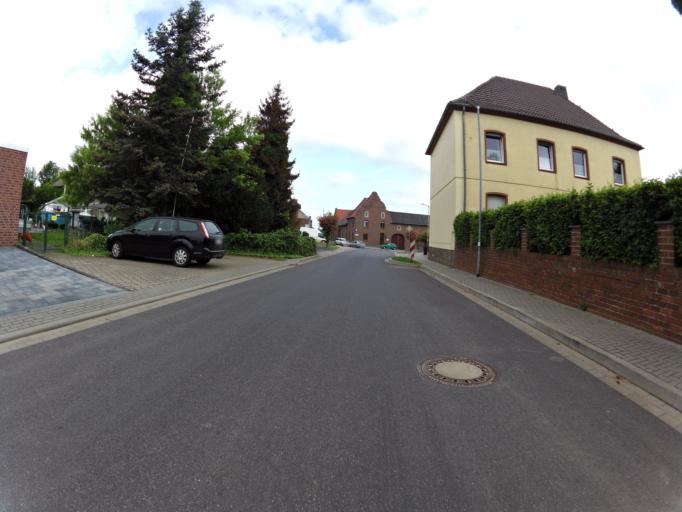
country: DE
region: North Rhine-Westphalia
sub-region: Regierungsbezirk Koln
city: Linnich
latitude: 50.9441
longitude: 6.2479
